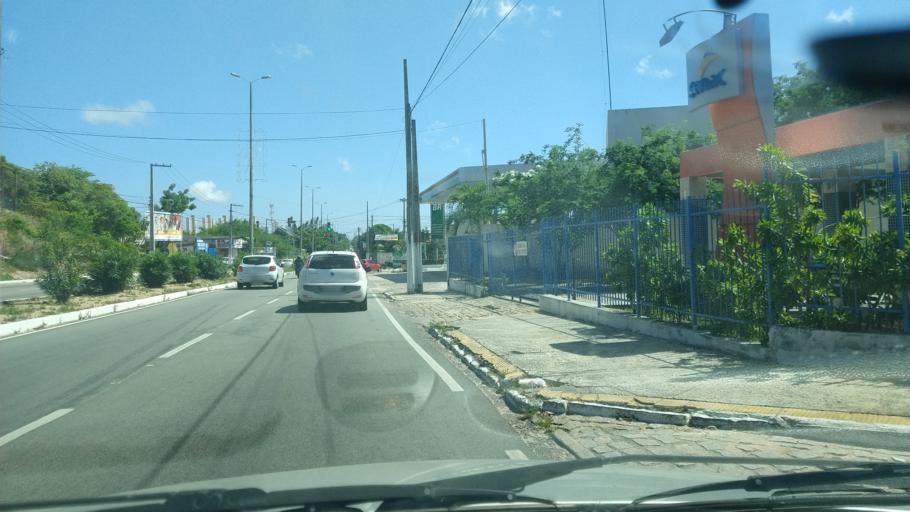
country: BR
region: Rio Grande do Norte
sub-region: Natal
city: Natal
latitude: -5.8621
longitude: -35.2053
